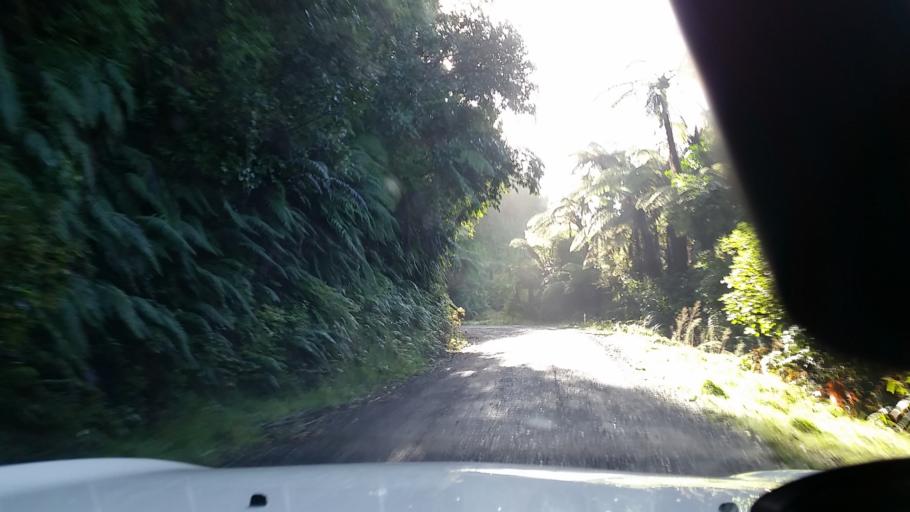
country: NZ
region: Bay of Plenty
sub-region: Kawerau District
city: Kawerau
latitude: -38.0293
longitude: 176.5570
